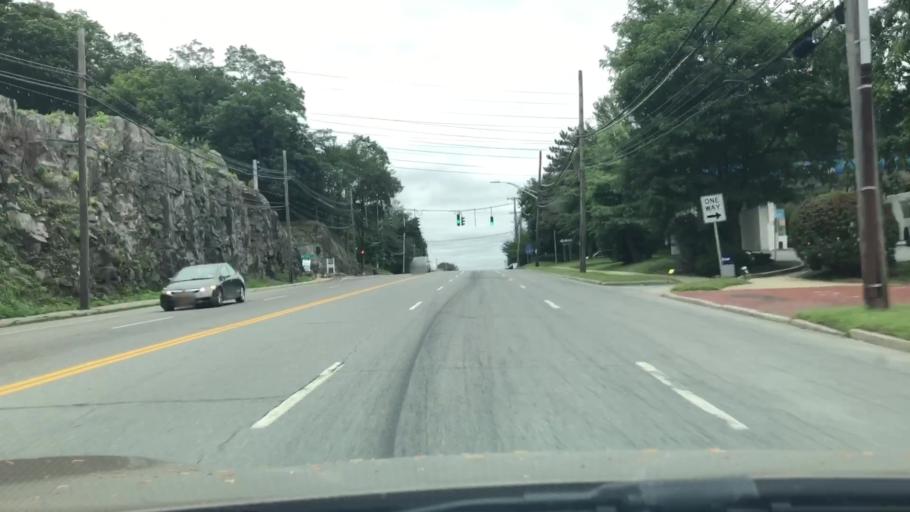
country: US
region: New York
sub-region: Westchester County
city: Elmsford
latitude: 41.0562
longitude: -73.8225
